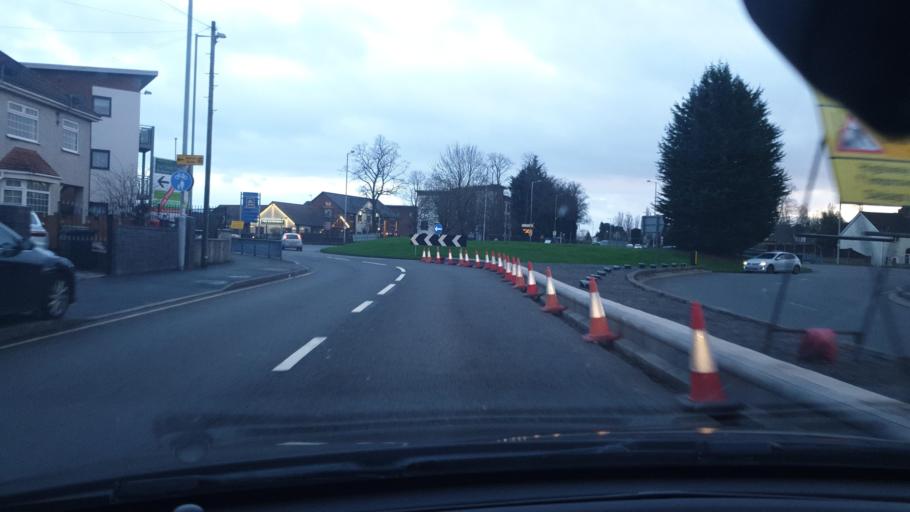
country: GB
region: England
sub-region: Wolverhampton
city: Wolverhampton
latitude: 52.6113
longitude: -2.1312
